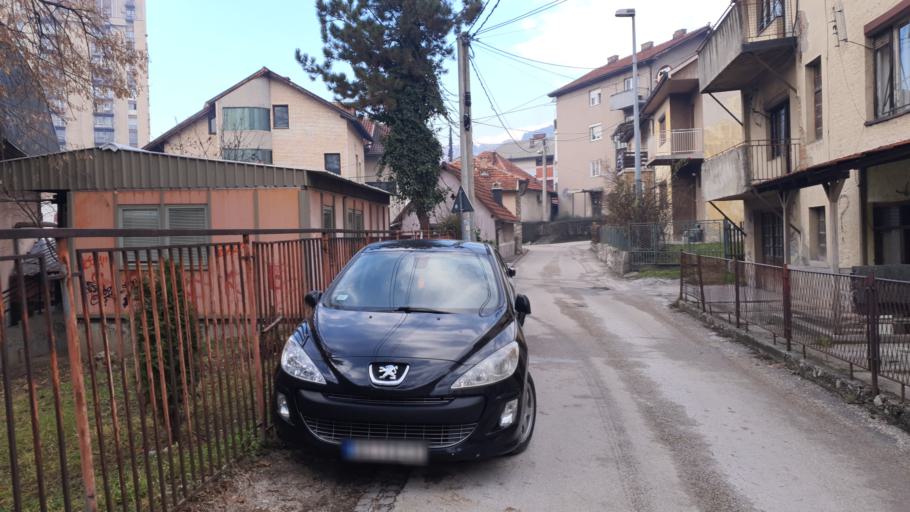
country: RS
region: Central Serbia
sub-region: Zlatiborski Okrug
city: Uzice
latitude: 43.8581
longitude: 19.8437
